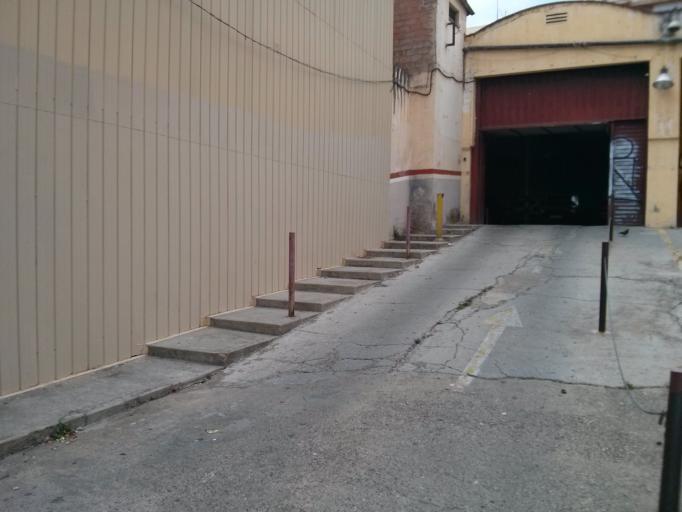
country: ES
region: Catalonia
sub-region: Provincia de Barcelona
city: Gracia
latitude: 41.4068
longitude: 2.1607
